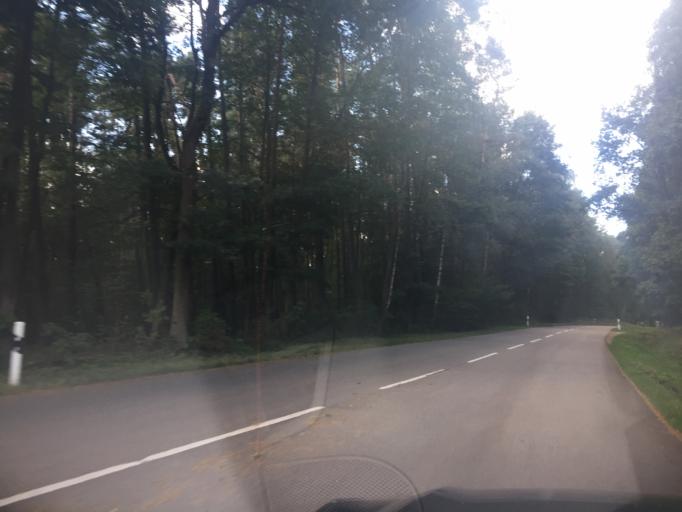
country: DE
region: Bavaria
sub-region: Upper Palatinate
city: Poppenricht
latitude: 49.4937
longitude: 11.8317
